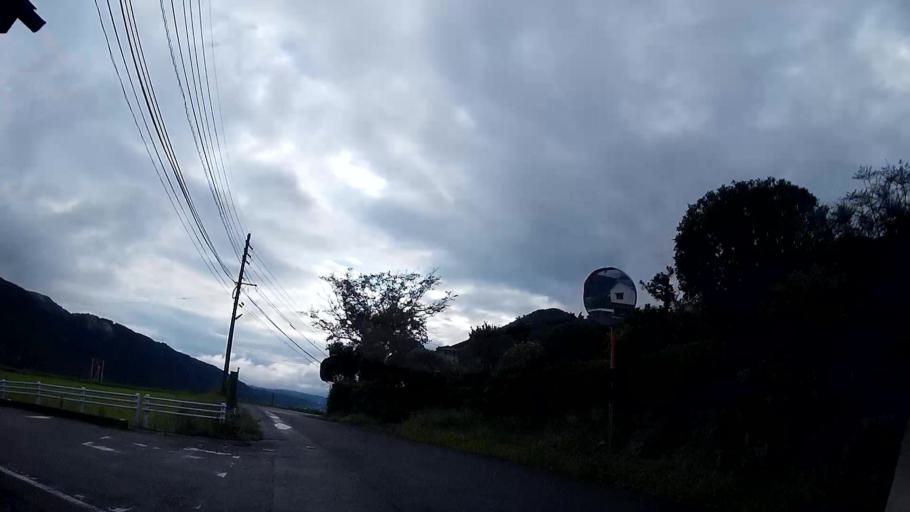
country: JP
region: Kumamoto
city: Ozu
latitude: 32.8797
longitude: 130.9654
